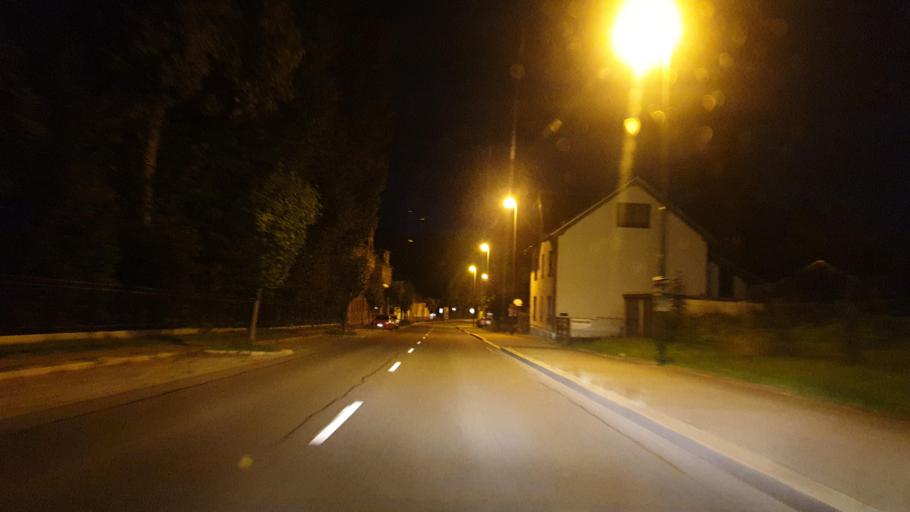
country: DE
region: Saxony
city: Auerbach
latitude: 50.4991
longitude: 12.3967
